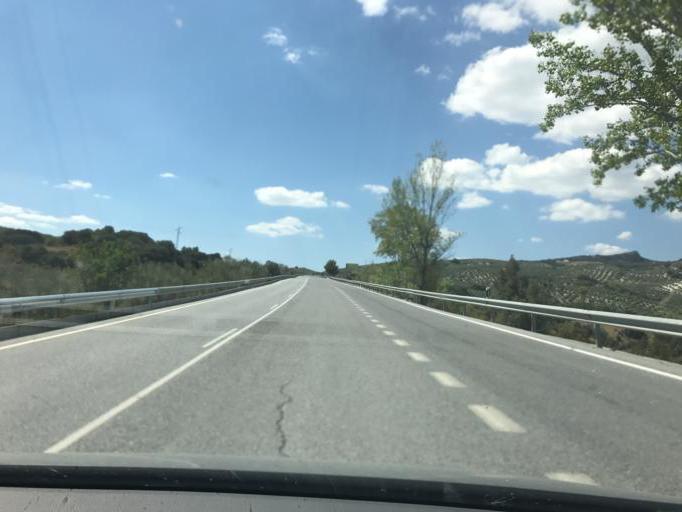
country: ES
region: Andalusia
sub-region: Provincia de Granada
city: Benalua de las Villas
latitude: 37.4279
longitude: -3.7326
